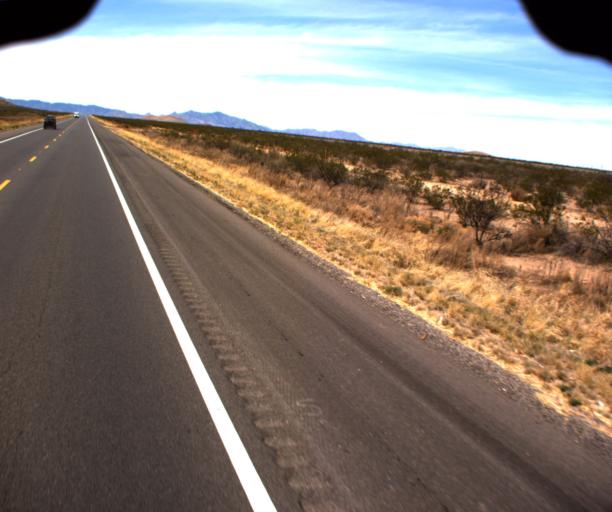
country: US
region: Arizona
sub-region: Cochise County
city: Willcox
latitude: 31.9056
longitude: -109.7271
